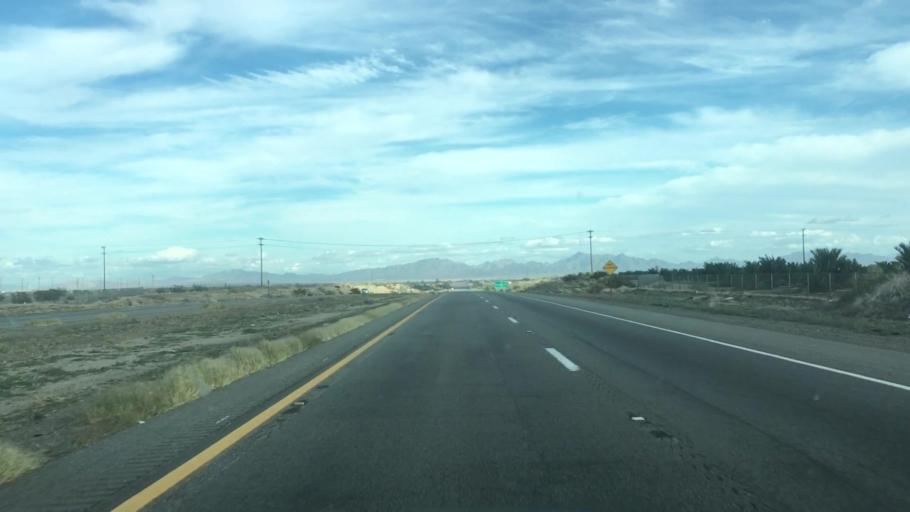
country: US
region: California
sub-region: Riverside County
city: Mesa Verde
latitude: 33.6065
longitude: -114.6832
